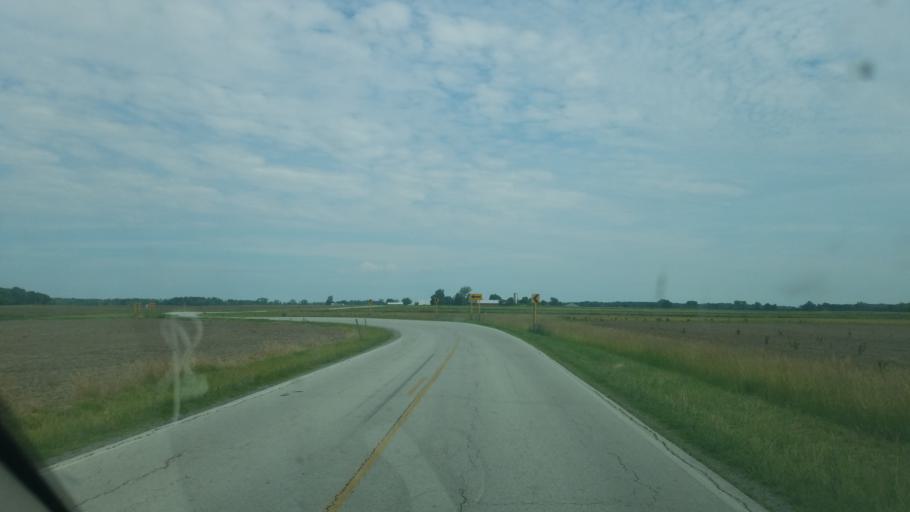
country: US
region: Ohio
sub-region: Seneca County
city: Fostoria
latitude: 41.0779
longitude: -83.4774
